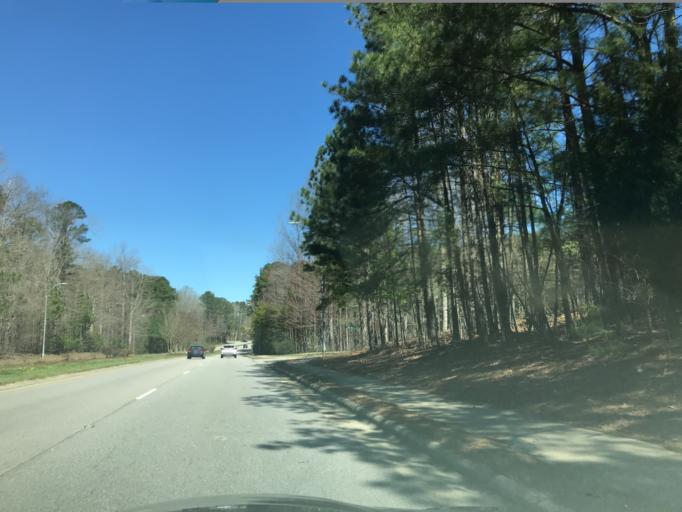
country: US
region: North Carolina
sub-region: Wake County
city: Garner
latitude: 35.7063
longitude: -78.6411
